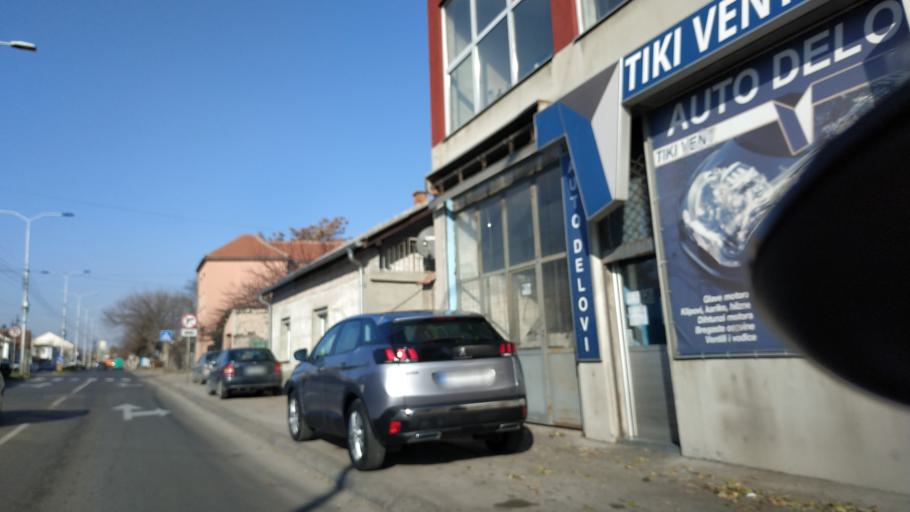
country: RS
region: Central Serbia
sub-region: Nisavski Okrug
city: Nis
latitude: 43.3269
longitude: 21.8894
